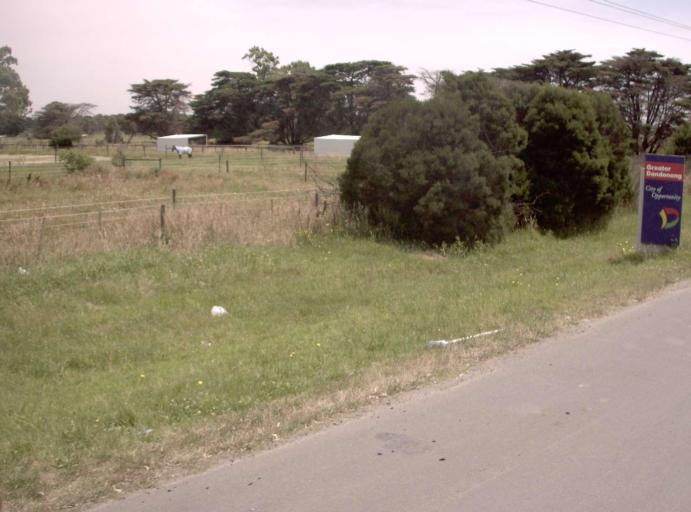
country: AU
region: Victoria
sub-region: Casey
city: Lynbrook
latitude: -38.0765
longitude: 145.2395
